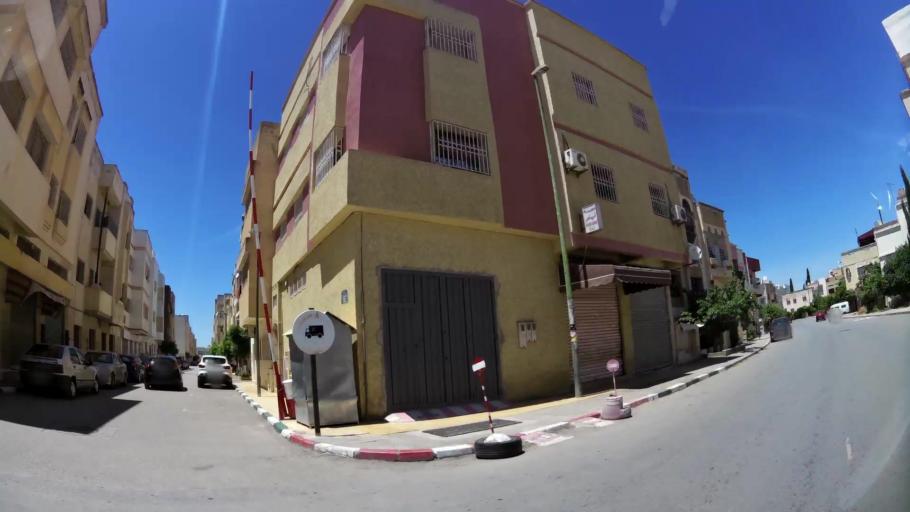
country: MA
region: Fes-Boulemane
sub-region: Fes
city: Fes
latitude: 34.0260
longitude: -5.0088
